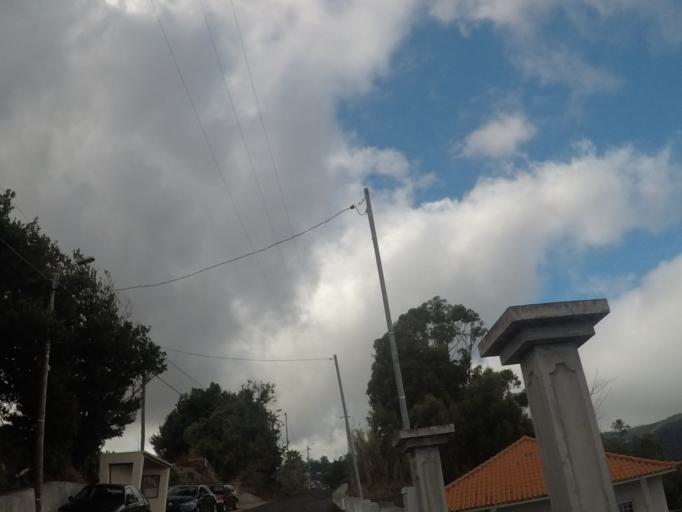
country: PT
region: Madeira
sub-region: Santa Cruz
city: Camacha
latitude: 32.6665
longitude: -16.8310
